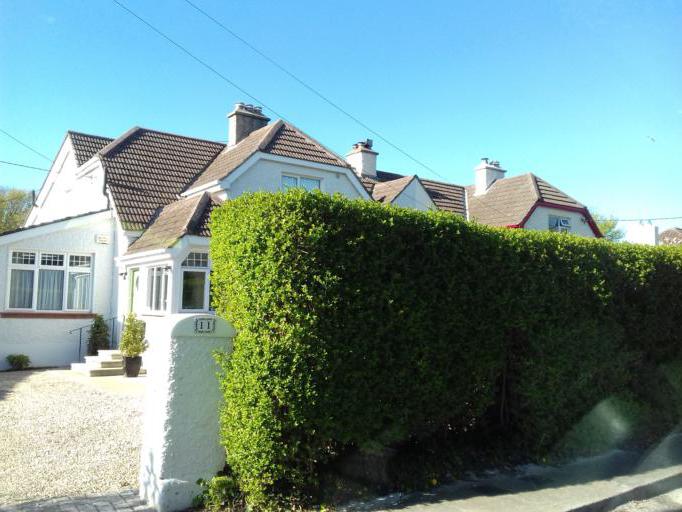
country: IE
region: Leinster
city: Sutton
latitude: 53.3792
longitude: -6.1012
